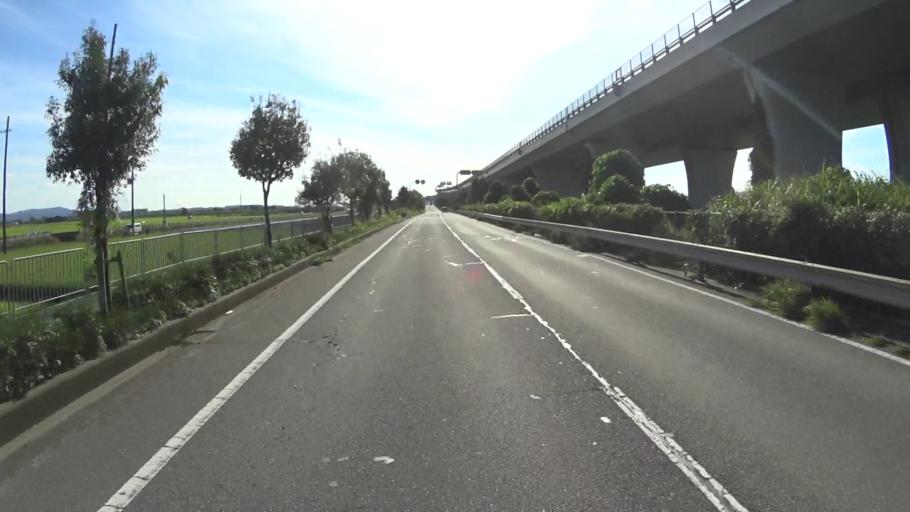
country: JP
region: Kyoto
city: Uji
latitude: 34.9011
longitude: 135.7610
